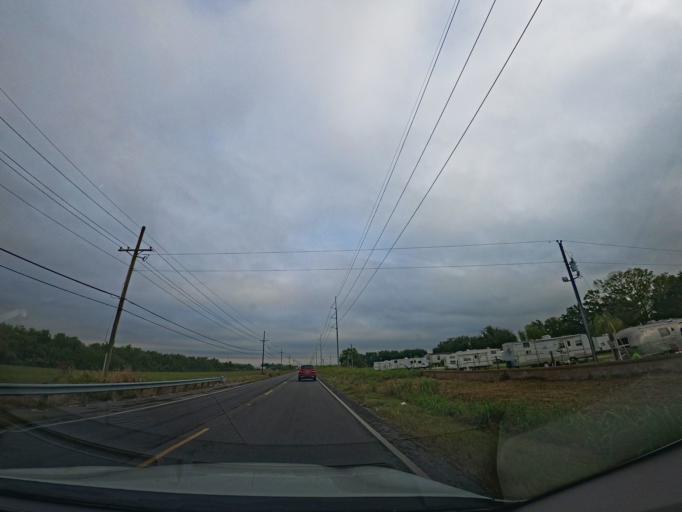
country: US
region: Louisiana
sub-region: Terrebonne Parish
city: Presquille
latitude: 29.5385
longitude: -90.6773
